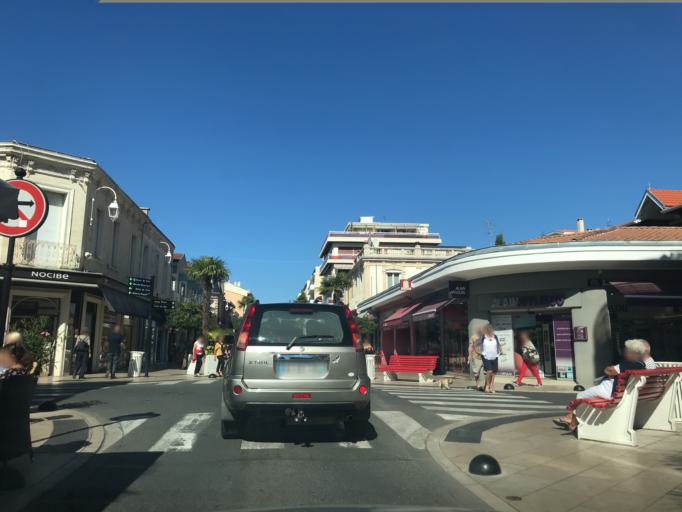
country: FR
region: Aquitaine
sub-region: Departement de la Gironde
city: Arcachon
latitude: 44.6605
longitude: -1.1684
